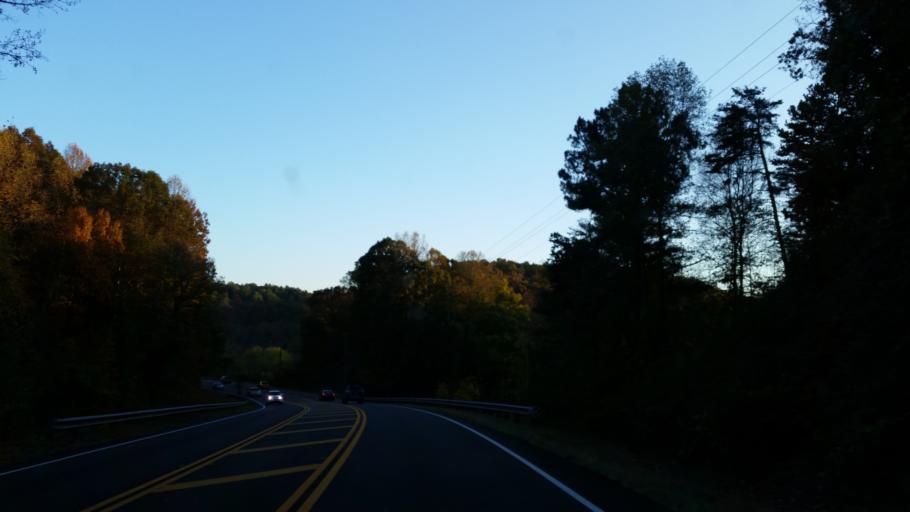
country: US
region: Georgia
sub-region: Lumpkin County
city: Dahlonega
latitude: 34.4753
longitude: -83.9795
